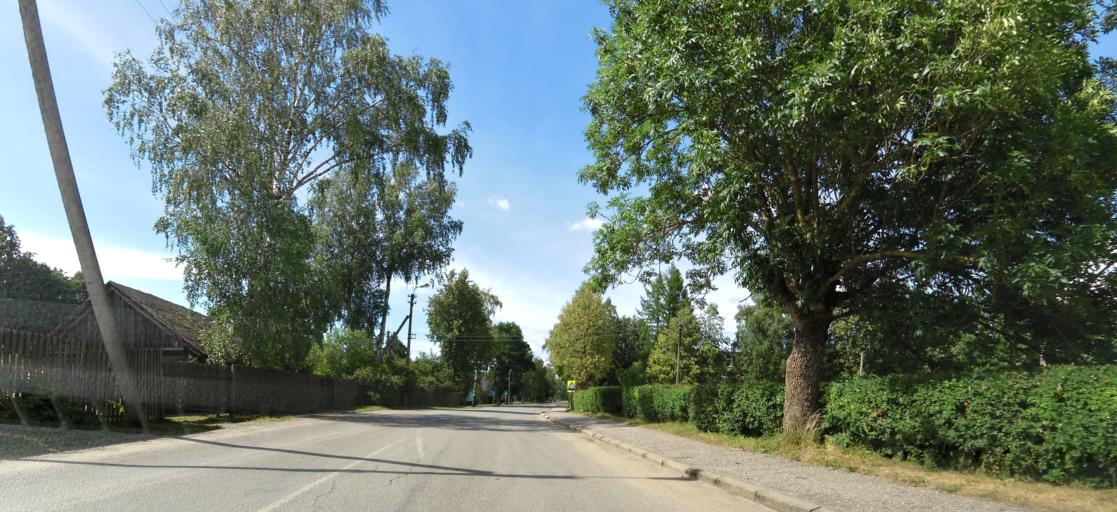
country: LT
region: Panevezys
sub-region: Birzai
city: Birzai
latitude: 56.1869
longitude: 24.6349
